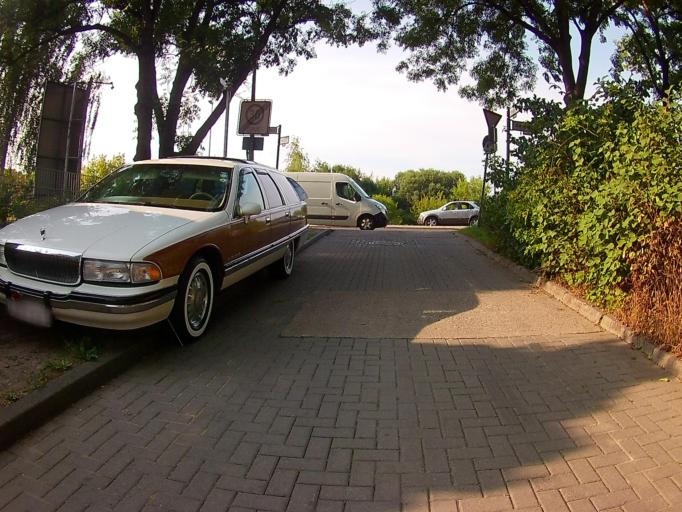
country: DE
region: Berlin
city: Kaulsdorf
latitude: 52.5050
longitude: 13.5779
